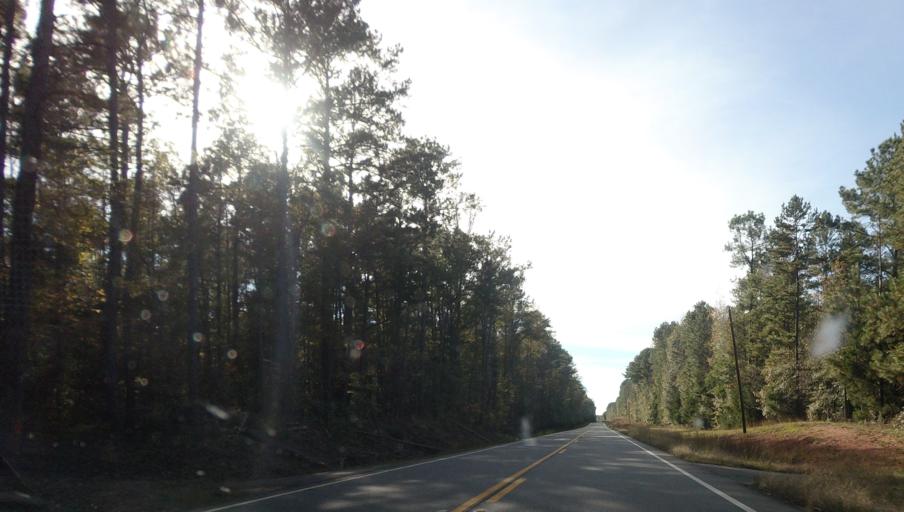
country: US
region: Georgia
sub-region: Taylor County
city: Butler
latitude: 32.7177
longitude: -84.2574
